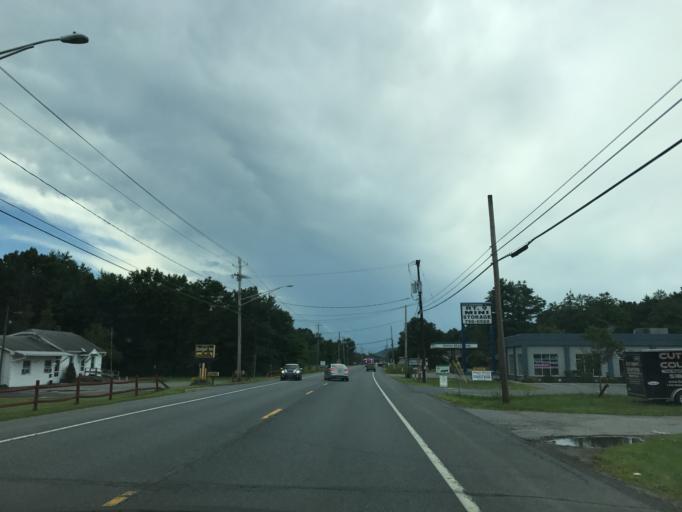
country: US
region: New York
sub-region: Warren County
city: West Glens Falls
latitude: 43.2552
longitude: -73.6632
